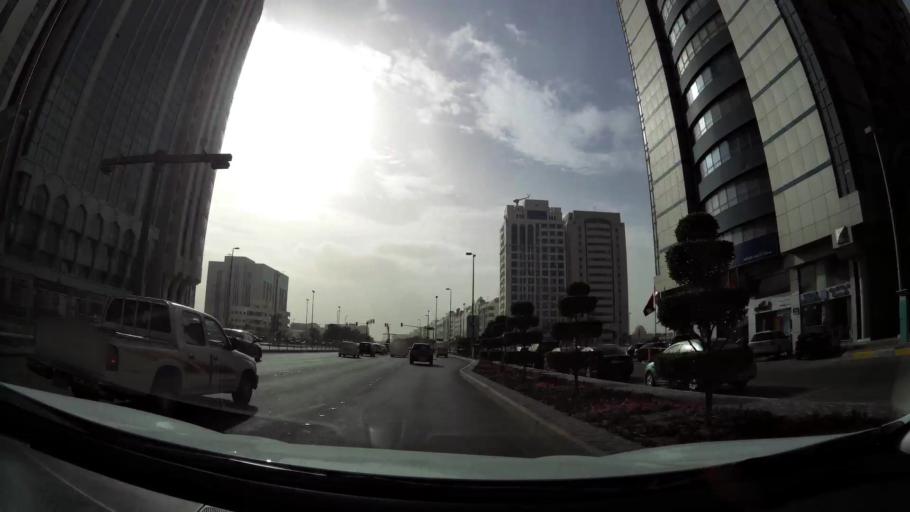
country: AE
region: Abu Dhabi
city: Abu Dhabi
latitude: 24.4840
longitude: 54.3750
